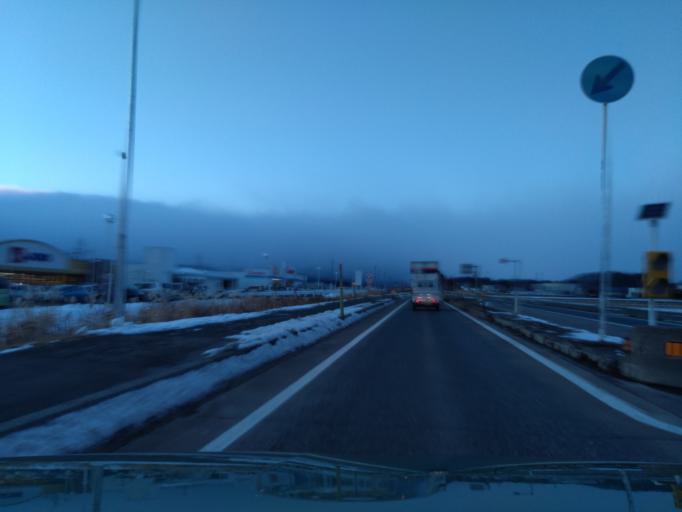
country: JP
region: Iwate
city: Shizukuishi
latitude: 39.6959
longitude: 140.9790
